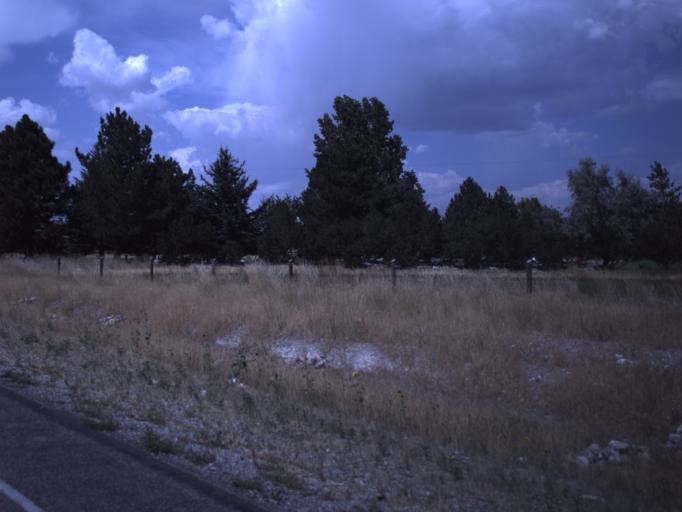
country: US
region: Utah
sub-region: Cache County
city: Mendon
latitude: 41.7604
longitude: -112.0066
